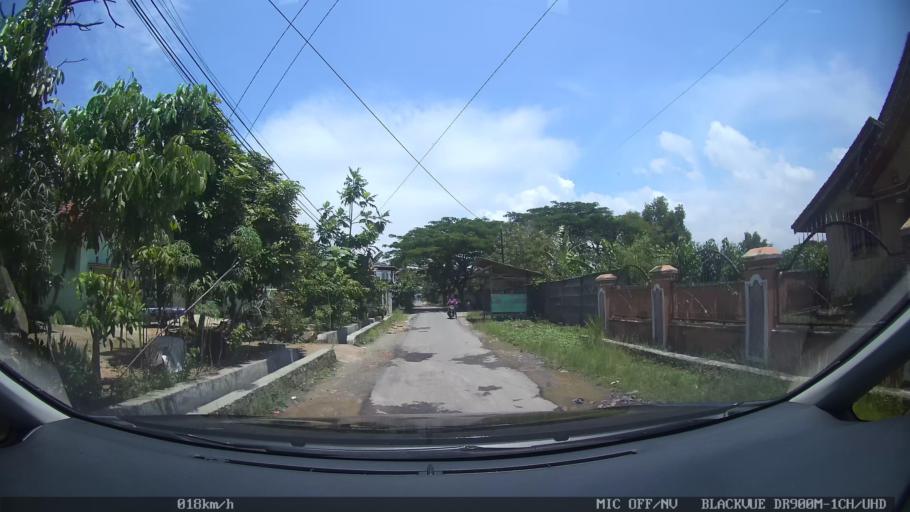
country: ID
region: Lampung
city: Kedaton
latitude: -5.3724
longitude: 105.2870
